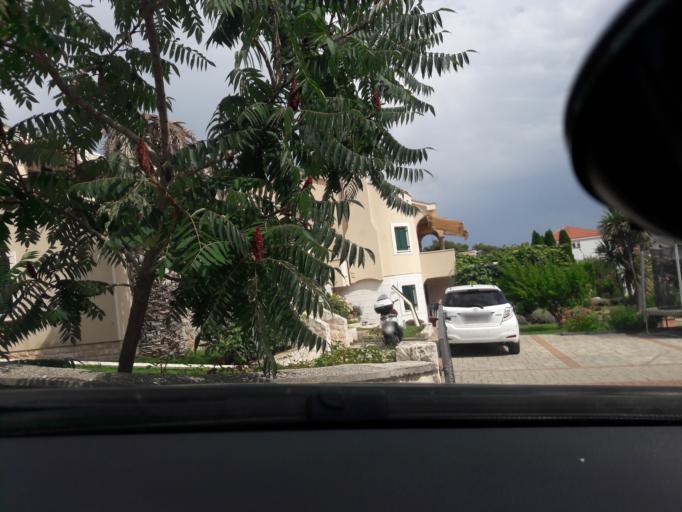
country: HR
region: Zadarska
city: Nin
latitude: 44.1683
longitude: 15.1845
